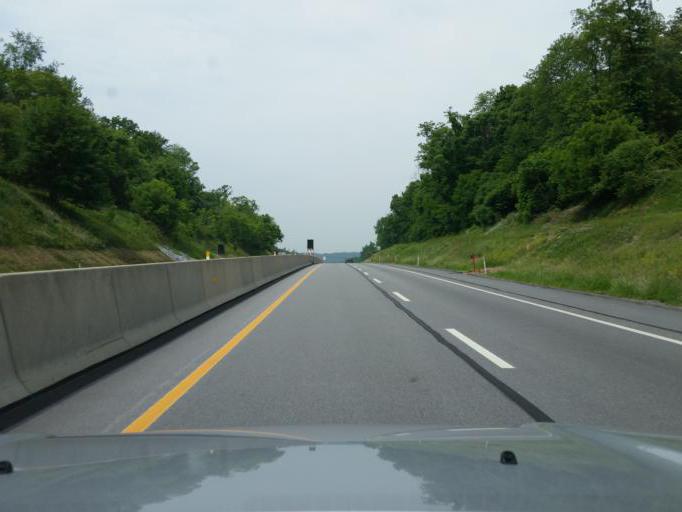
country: US
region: Pennsylvania
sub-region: Cumberland County
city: Lower Allen
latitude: 40.2060
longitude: -76.8935
